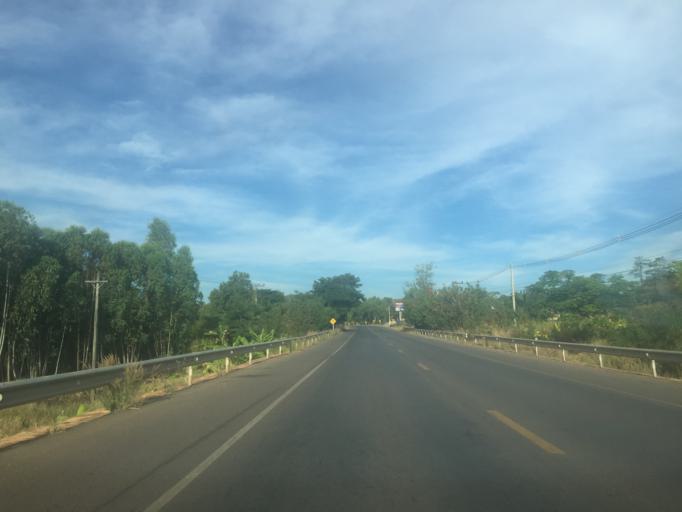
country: TH
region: Changwat Udon Thani
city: Si That
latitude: 16.9677
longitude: 103.2423
